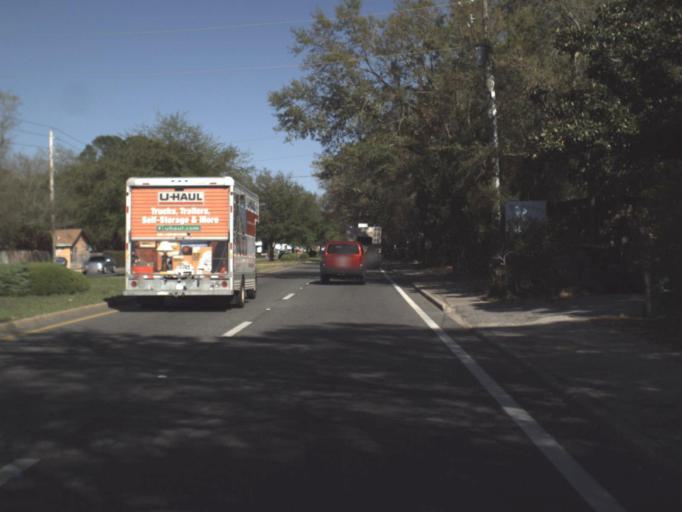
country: US
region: Florida
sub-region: Okaloosa County
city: Mary Esther
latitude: 30.4082
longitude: -86.6438
